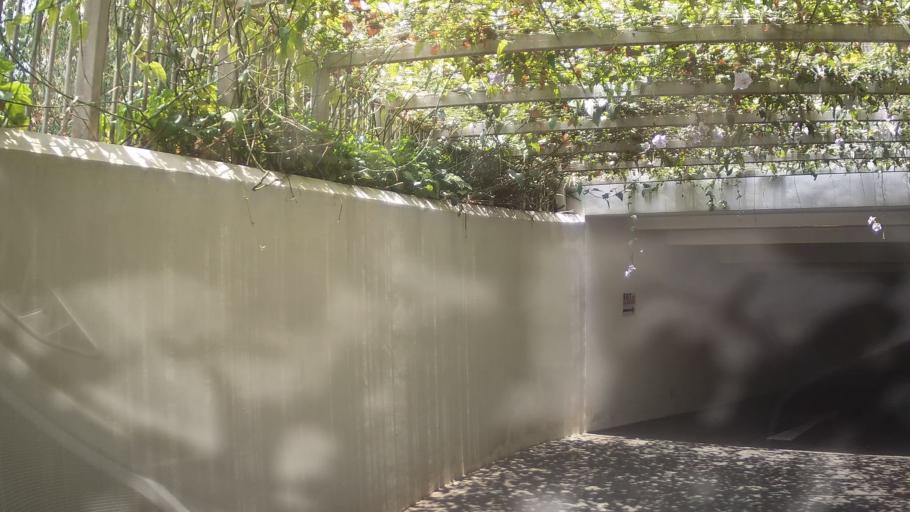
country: SG
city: Singapore
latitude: 1.2968
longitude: 103.8424
